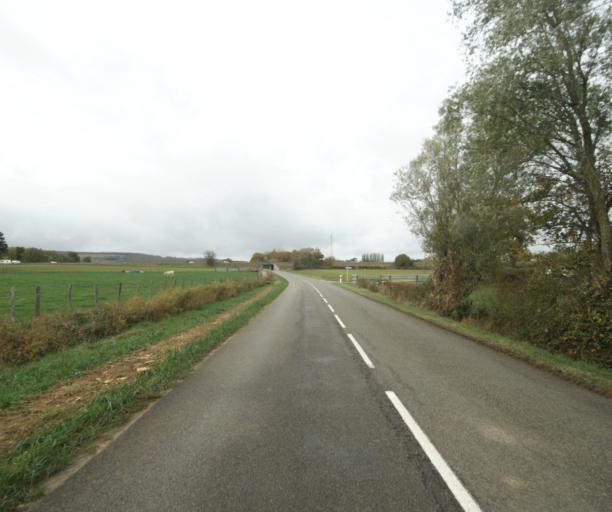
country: FR
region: Rhone-Alpes
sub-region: Departement de l'Ain
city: Pont-de-Vaux
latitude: 46.4599
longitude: 4.8803
